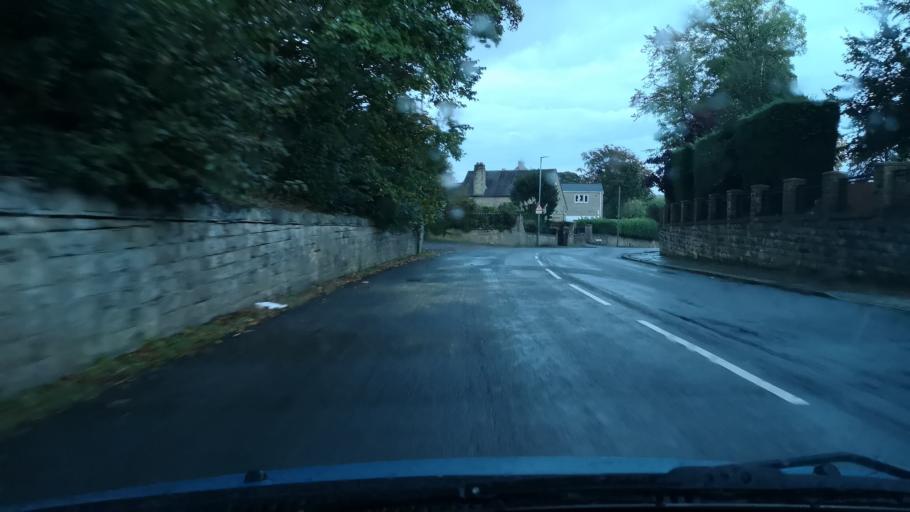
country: GB
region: England
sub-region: Kirklees
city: Batley
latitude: 53.7232
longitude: -1.6342
